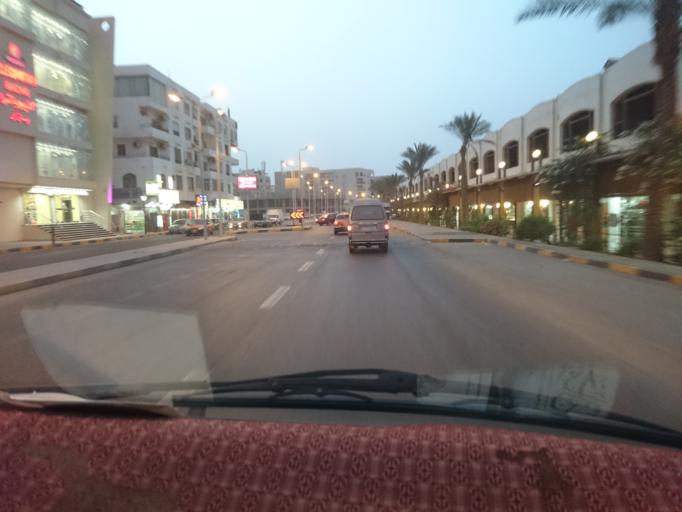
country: EG
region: Red Sea
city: Hurghada
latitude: 27.2393
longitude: 33.8450
